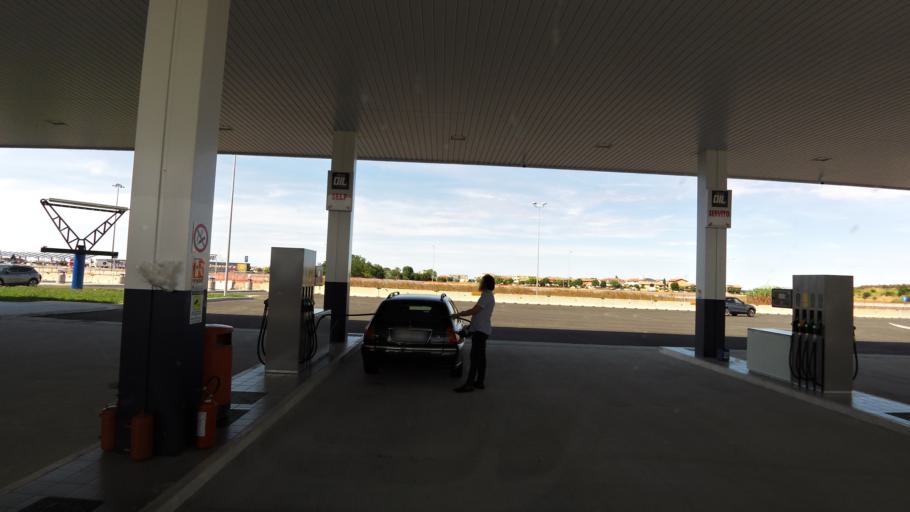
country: IT
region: The Marches
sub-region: Provincia di Pesaro e Urbino
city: Marotta
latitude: 43.7537
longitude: 13.1466
